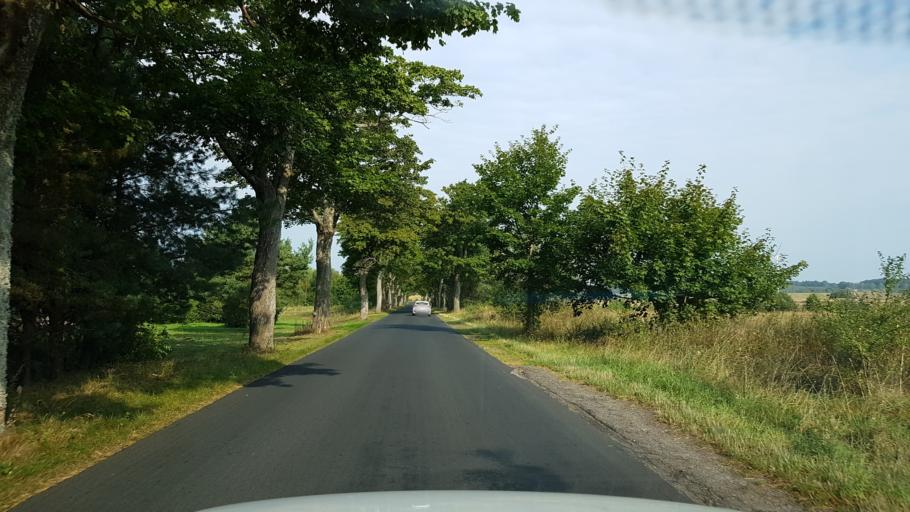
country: PL
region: West Pomeranian Voivodeship
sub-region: Powiat slawienski
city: Slawno
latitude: 54.4535
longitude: 16.5934
